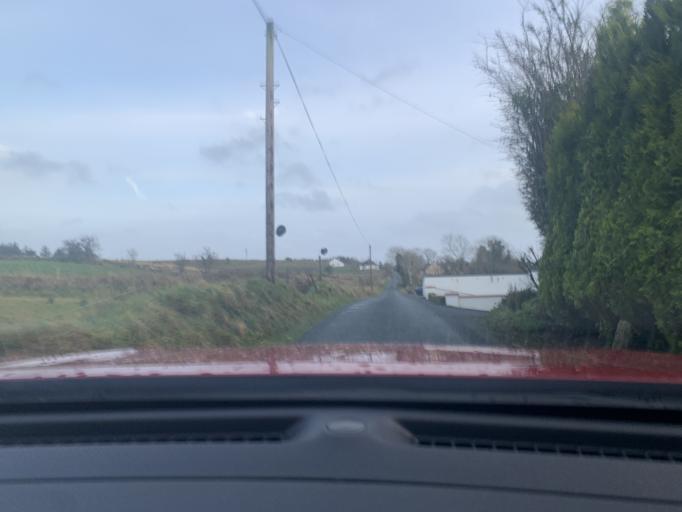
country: IE
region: Connaught
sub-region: Roscommon
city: Ballaghaderreen
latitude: 53.9539
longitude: -8.5262
